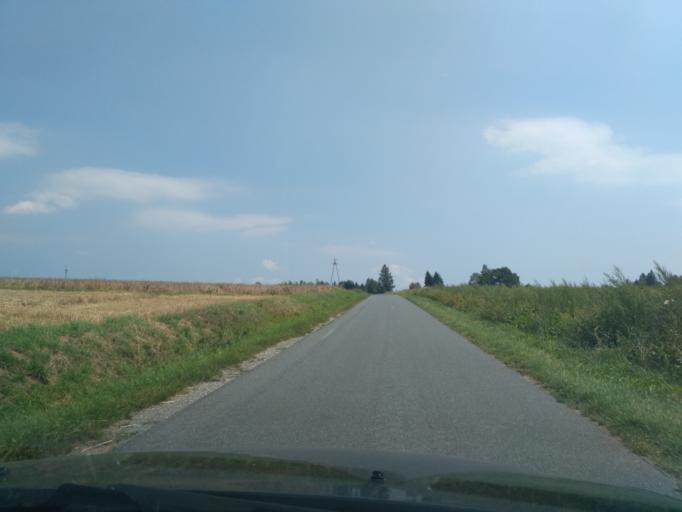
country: PL
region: Subcarpathian Voivodeship
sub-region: Powiat strzyzowski
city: Wysoka Strzyzowska
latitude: 49.8618
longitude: 21.7147
